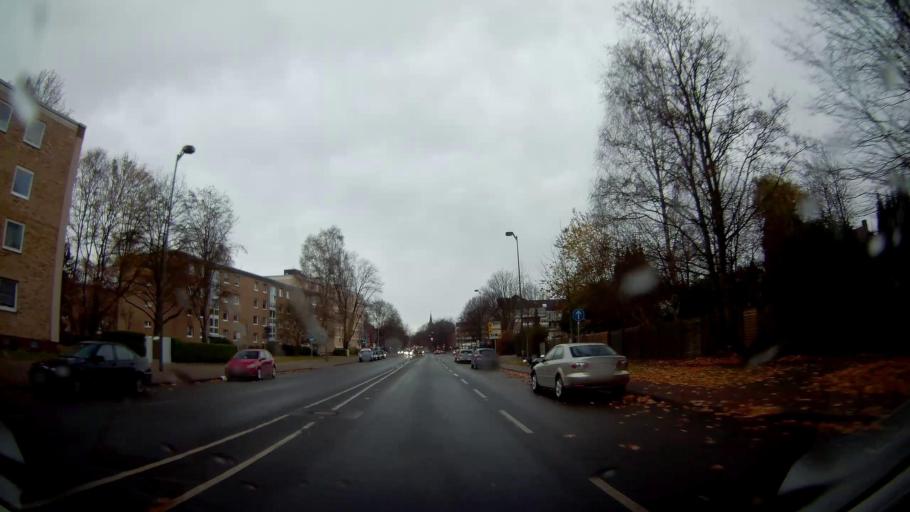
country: DE
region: North Rhine-Westphalia
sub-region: Regierungsbezirk Munster
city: Gelsenkirchen
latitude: 51.5063
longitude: 7.0783
